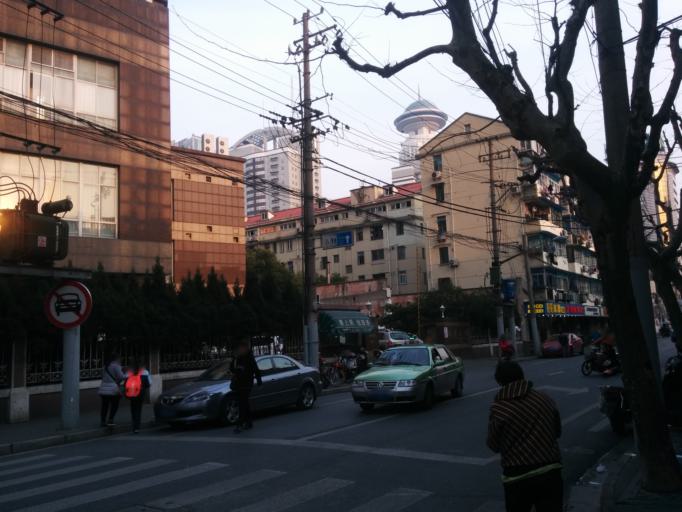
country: CN
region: Shanghai Shi
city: Shanghai
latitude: 31.2396
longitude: 121.4645
